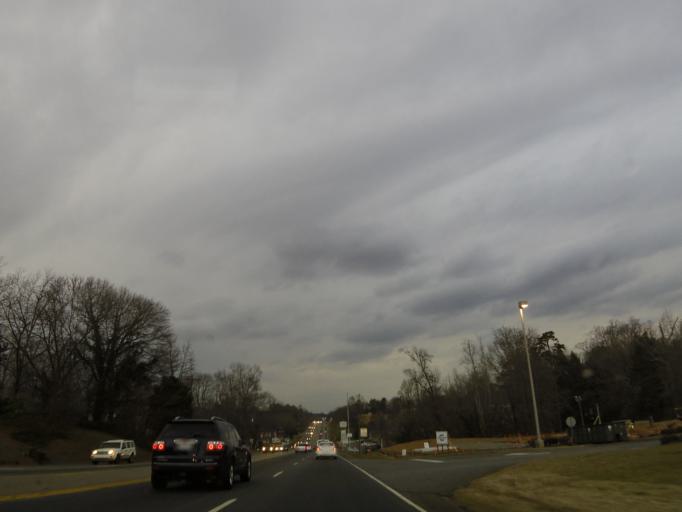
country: US
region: South Carolina
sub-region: Greenville County
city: Sans Souci
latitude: 34.8932
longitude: -82.4080
